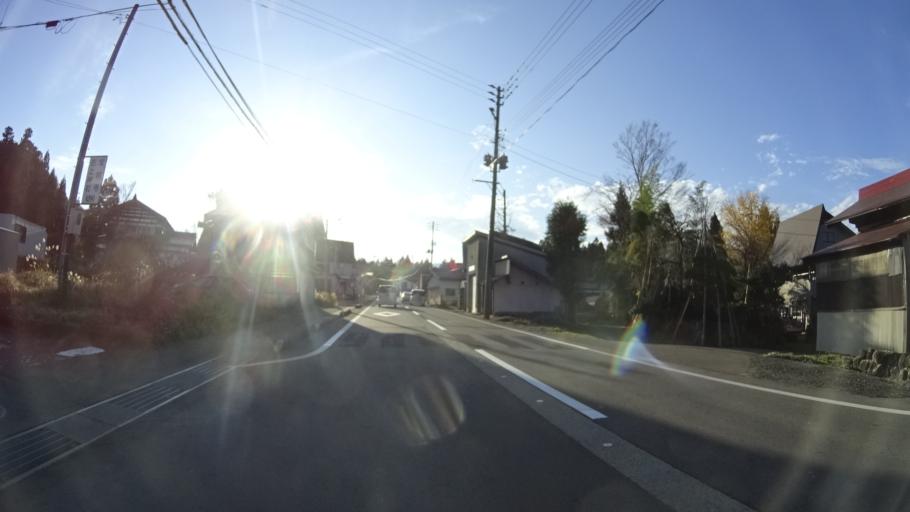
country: JP
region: Niigata
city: Shiozawa
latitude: 37.0021
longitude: 138.8325
